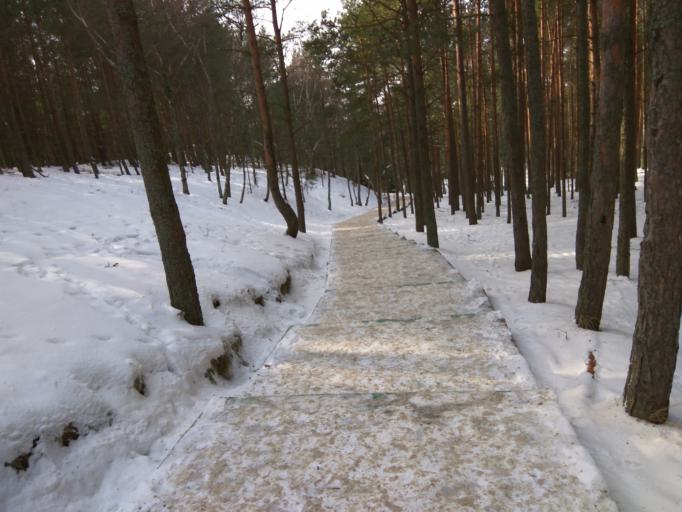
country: LT
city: Nida
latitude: 55.2210
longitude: 20.8991
